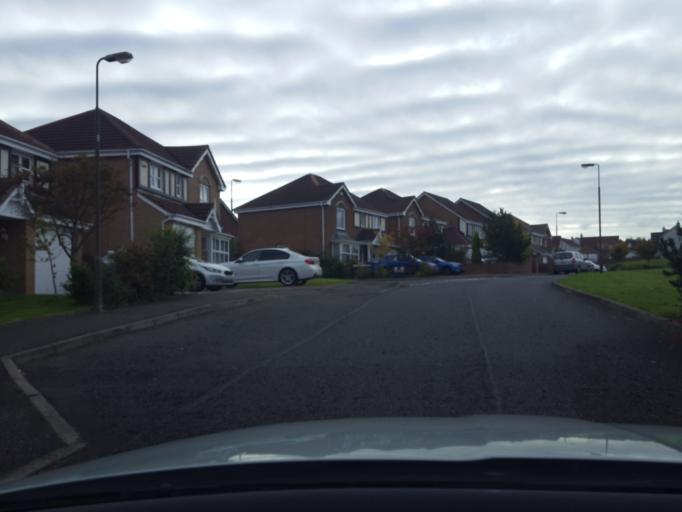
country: GB
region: Scotland
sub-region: West Lothian
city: Livingston
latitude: 55.8736
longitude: -3.5286
